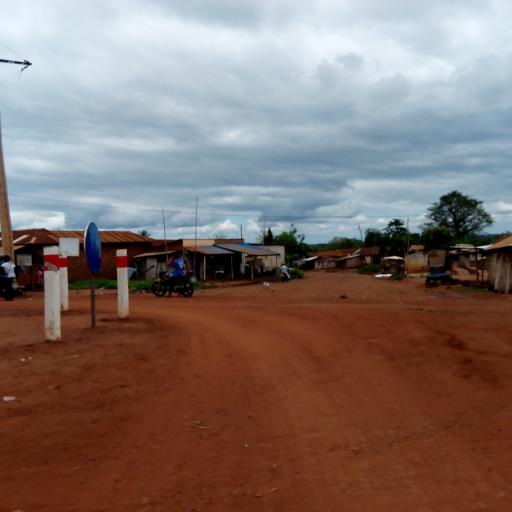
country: TG
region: Maritime
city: Tsevie
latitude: 6.3406
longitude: 1.1105
